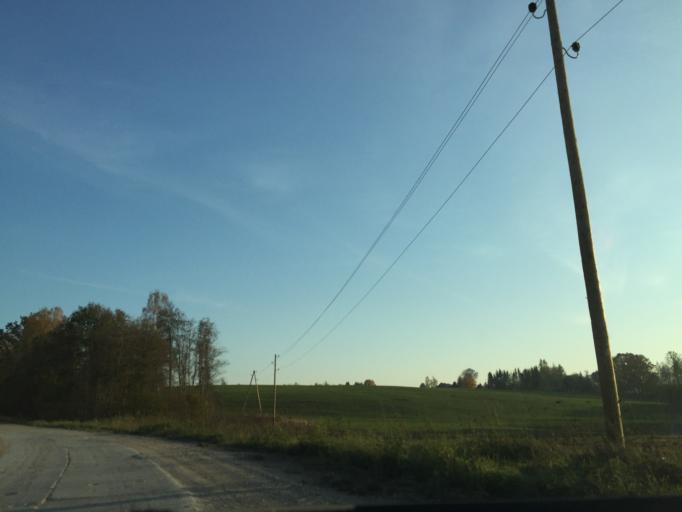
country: LV
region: Vainode
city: Vainode
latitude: 56.5550
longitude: 21.8402
